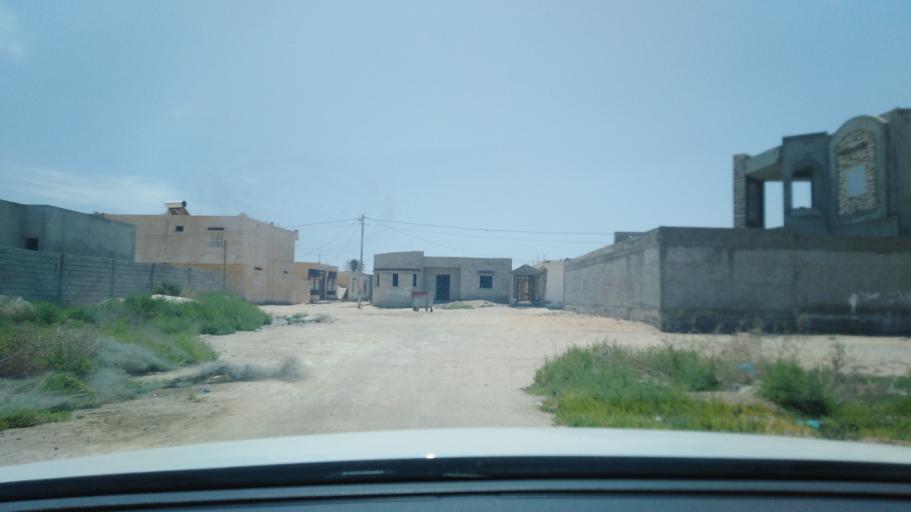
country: TN
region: Qabis
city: Gabes
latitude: 33.9456
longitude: 10.0740
